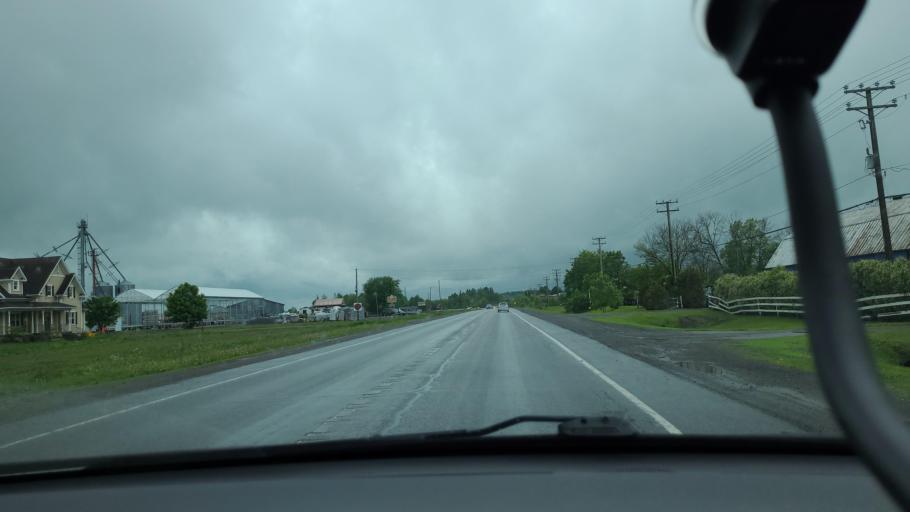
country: CA
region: Quebec
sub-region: Laurentides
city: Saint-Colomban
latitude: 45.7277
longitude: -74.0658
